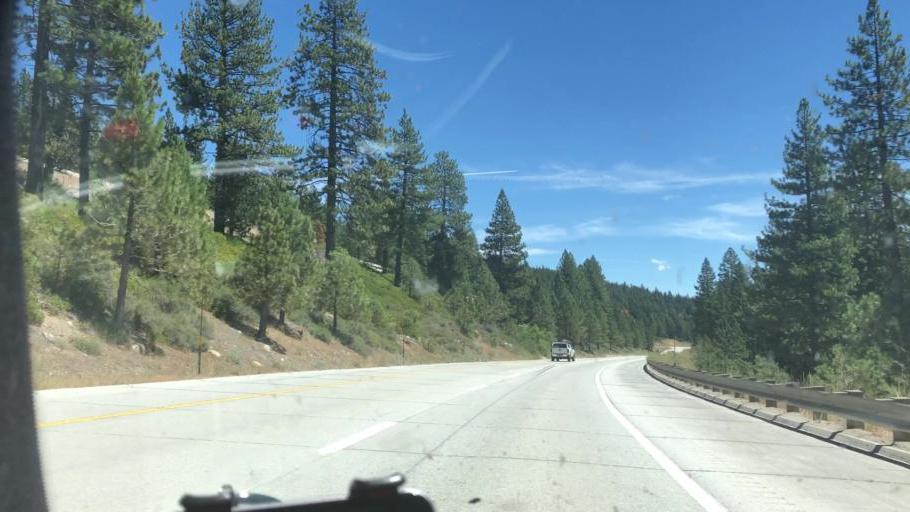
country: US
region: California
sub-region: Nevada County
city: Truckee
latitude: 39.3306
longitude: -120.2571
